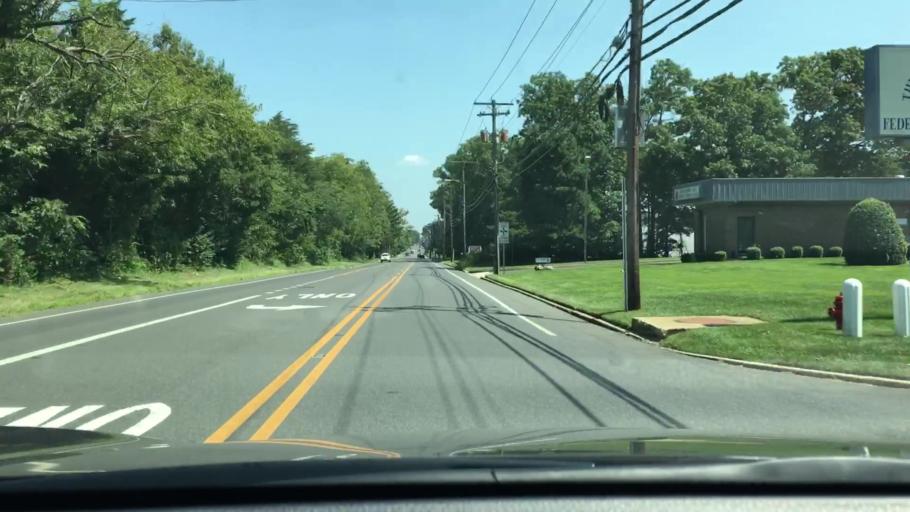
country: US
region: New Jersey
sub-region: Cumberland County
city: Millville
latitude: 39.3788
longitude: -75.0745
